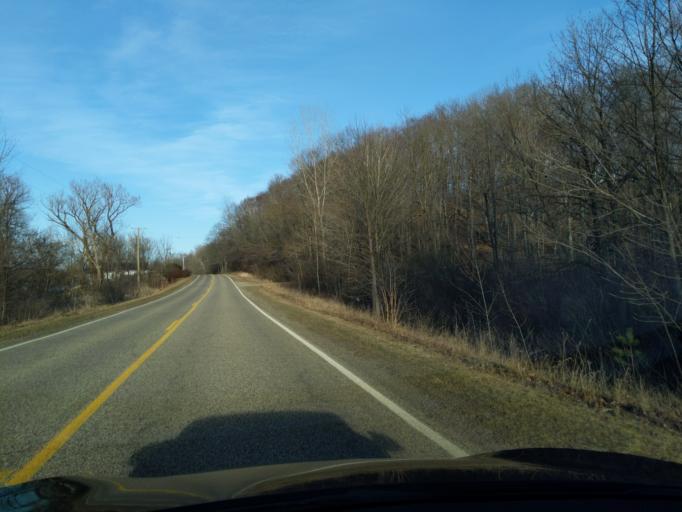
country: US
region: Michigan
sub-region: Ionia County
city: Ionia
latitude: 42.9603
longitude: -85.1031
